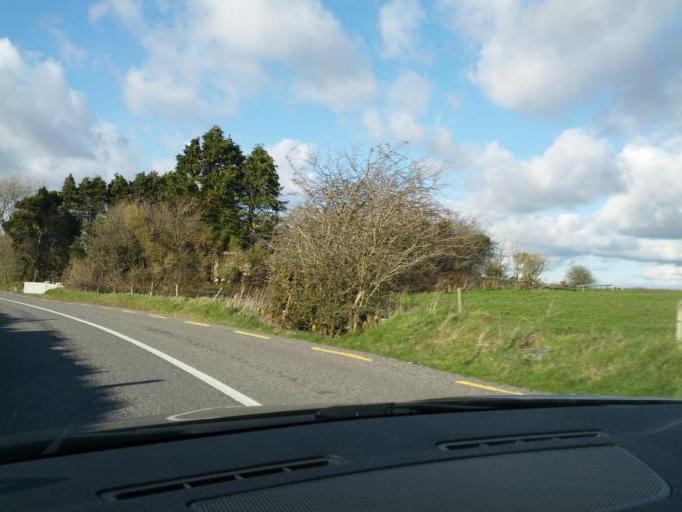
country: IE
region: Connaught
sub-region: Roscommon
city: Castlerea
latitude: 53.5794
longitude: -8.5619
